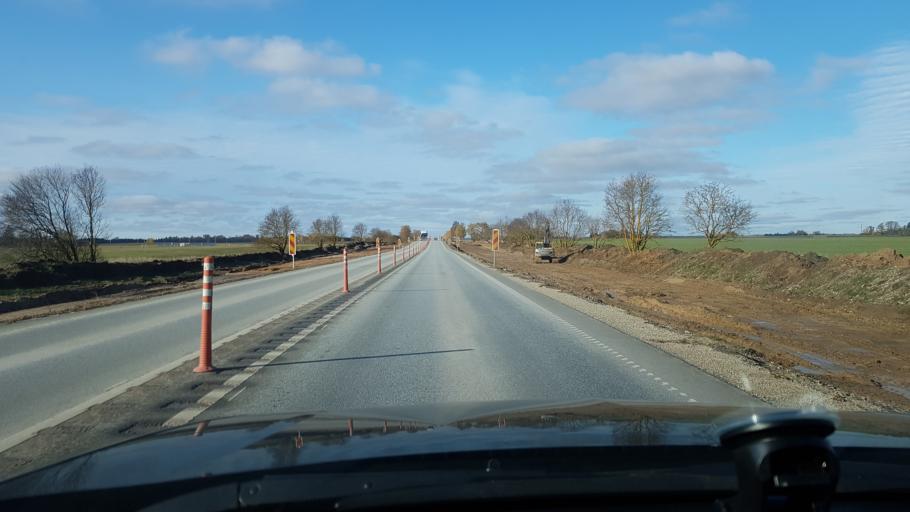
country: EE
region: Laeaene-Virumaa
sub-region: Haljala vald
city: Haljala
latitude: 59.4269
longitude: 26.2438
